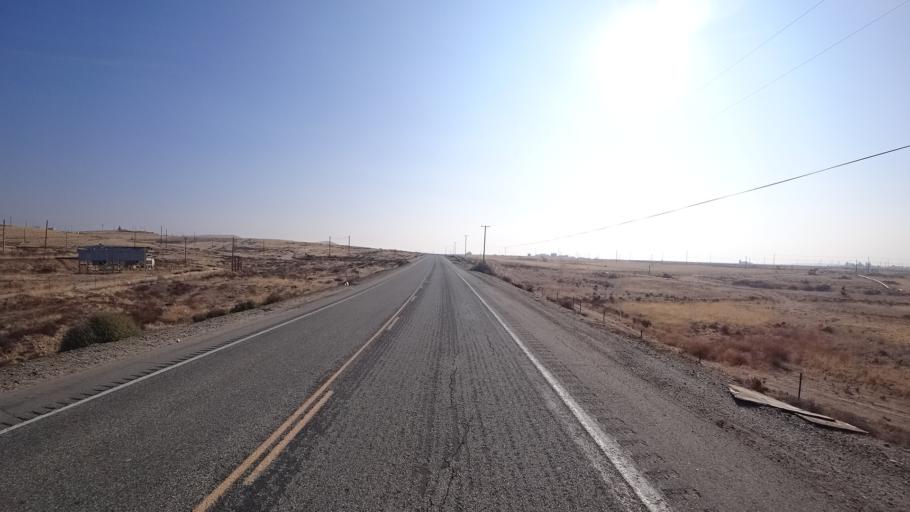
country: US
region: California
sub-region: Kern County
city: Lamont
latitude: 35.3780
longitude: -118.8486
